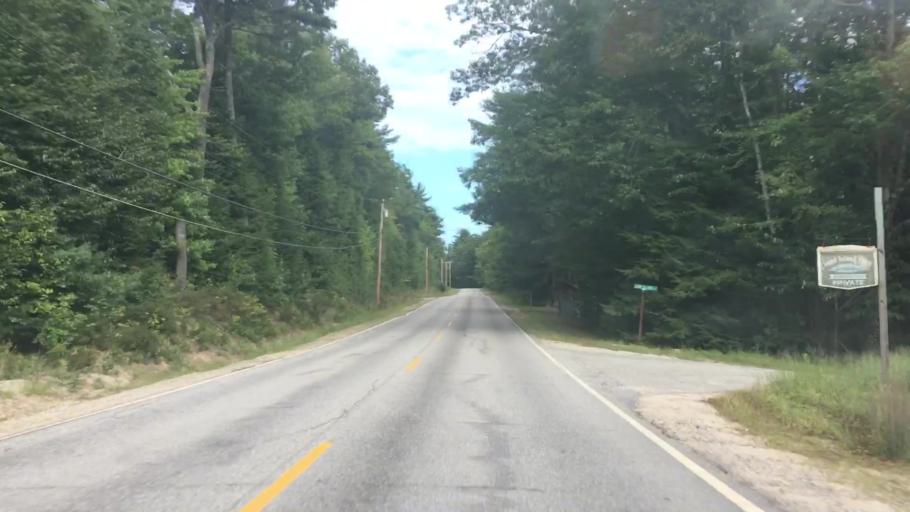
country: US
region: Maine
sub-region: Oxford County
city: Oxford
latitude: 44.0957
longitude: -70.5191
